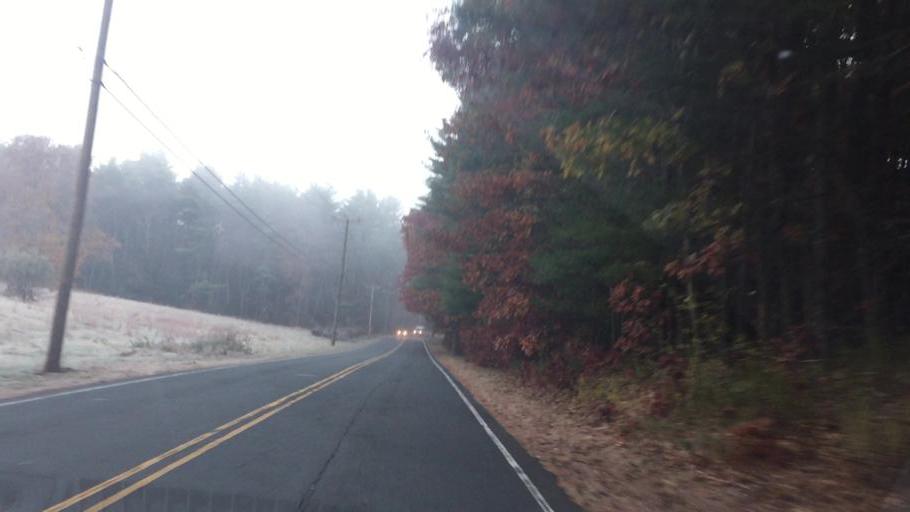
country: US
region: Massachusetts
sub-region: Hampshire County
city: Southampton
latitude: 42.2153
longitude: -72.6906
